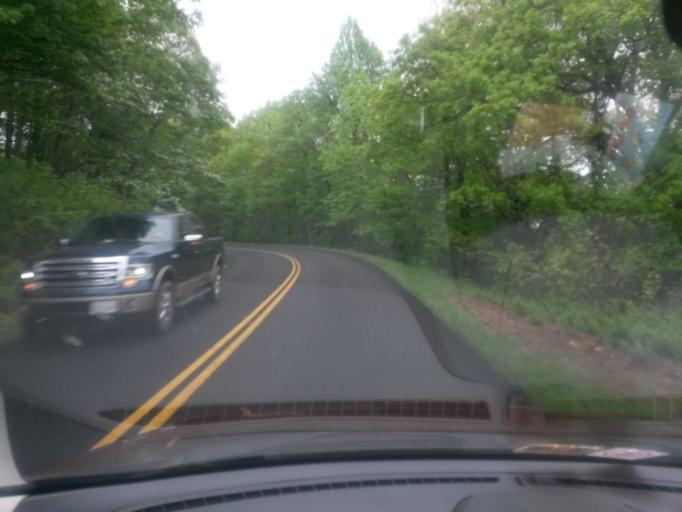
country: US
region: Virginia
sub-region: Floyd County
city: Floyd
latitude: 36.8265
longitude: -80.3460
